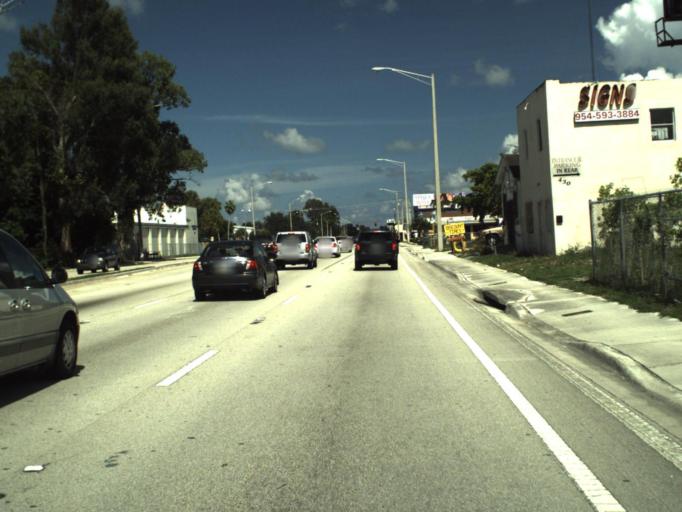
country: US
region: Florida
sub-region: Broward County
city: Carver Ranches
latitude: 25.9954
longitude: -80.1865
